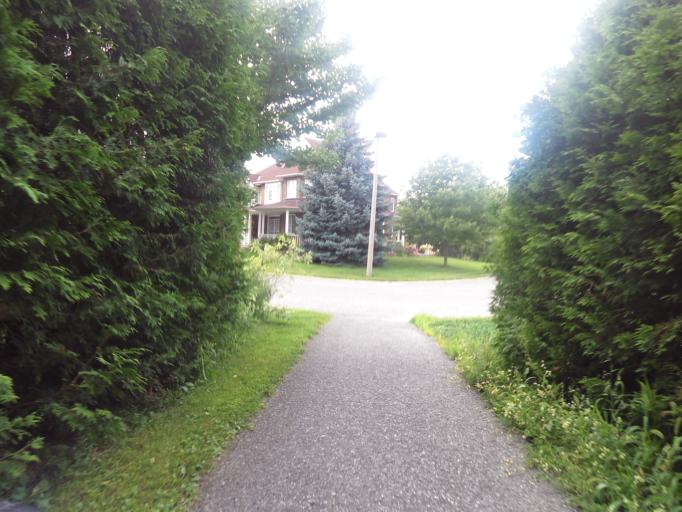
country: CA
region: Ontario
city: Bells Corners
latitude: 45.3254
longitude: -75.9192
